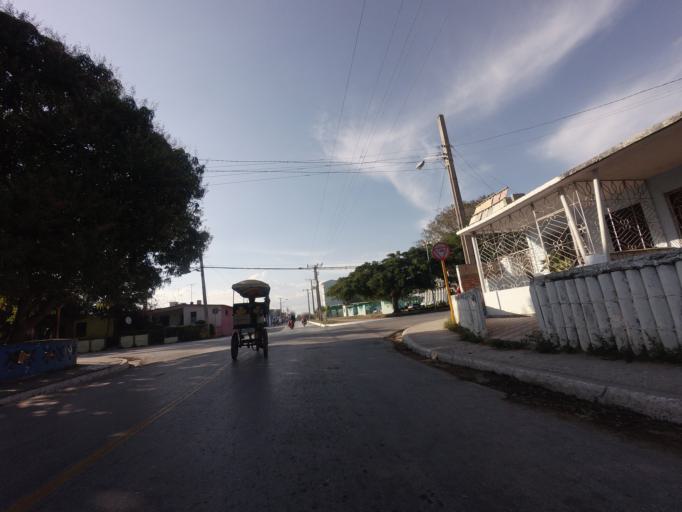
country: CU
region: Ciego de Avila
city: Ciego de Avila
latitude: 21.8459
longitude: -78.7679
